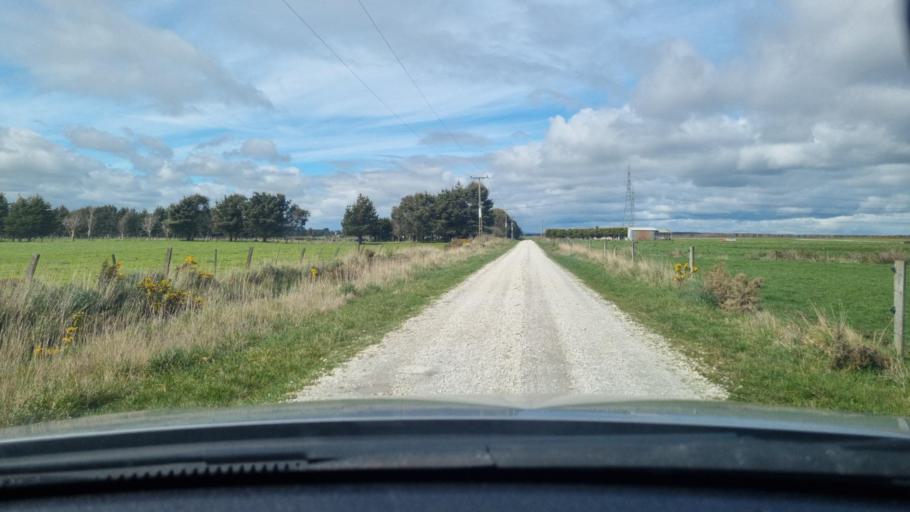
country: NZ
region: Southland
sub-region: Invercargill City
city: Invercargill
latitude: -46.4768
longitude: 168.4300
